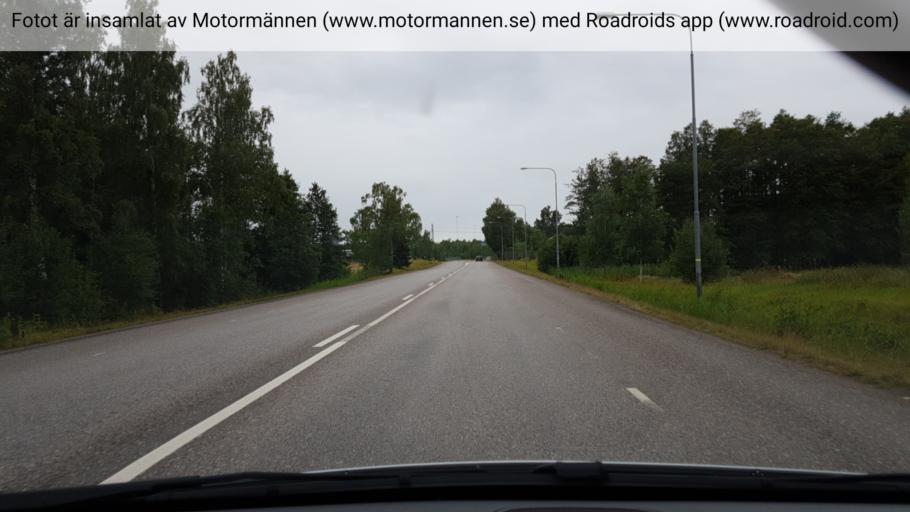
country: SE
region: Vaestra Goetaland
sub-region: Tibro Kommun
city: Tibro
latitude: 58.4225
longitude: 14.1342
